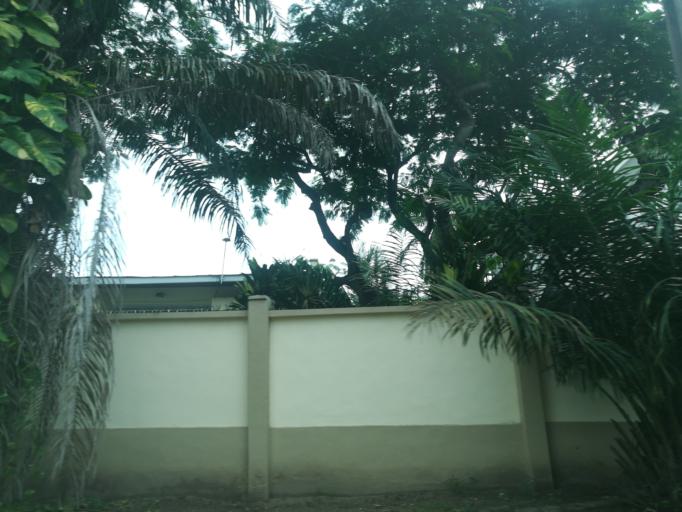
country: NG
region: Lagos
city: Ikoyi
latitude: 6.4353
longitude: 3.4155
